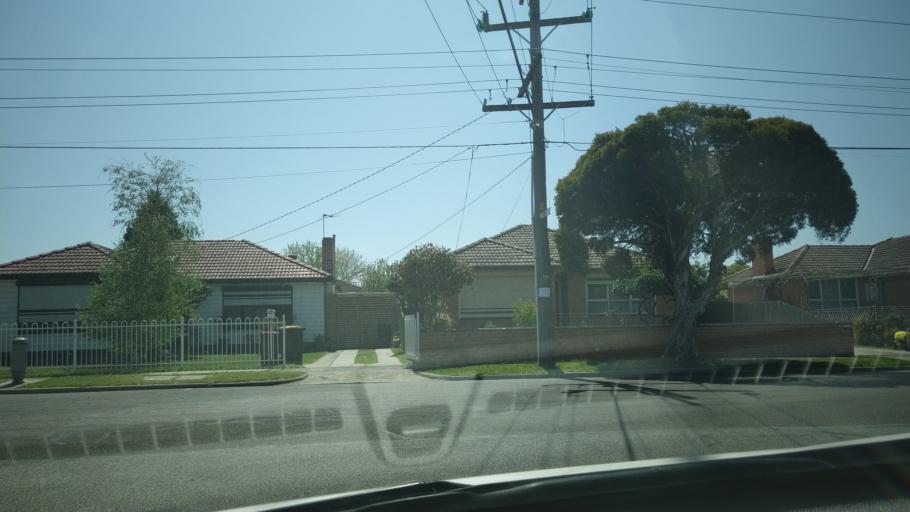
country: AU
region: Victoria
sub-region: Greater Dandenong
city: Noble Park
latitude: -37.9676
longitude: 145.1635
